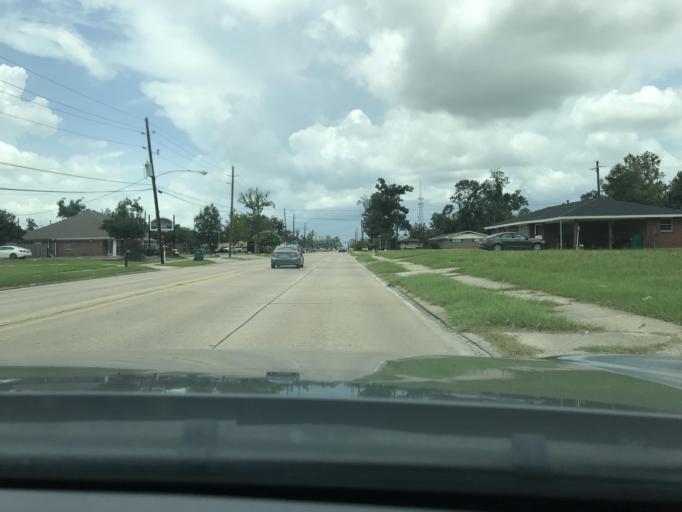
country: US
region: Louisiana
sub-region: Calcasieu Parish
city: Sulphur
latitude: 30.2277
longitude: -93.3298
